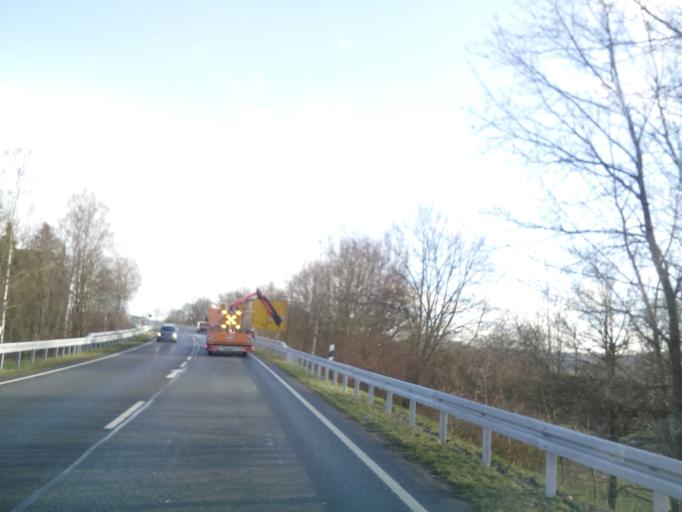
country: DE
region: Bavaria
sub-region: Upper Franconia
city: Mainleus
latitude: 50.1073
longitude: 11.3596
